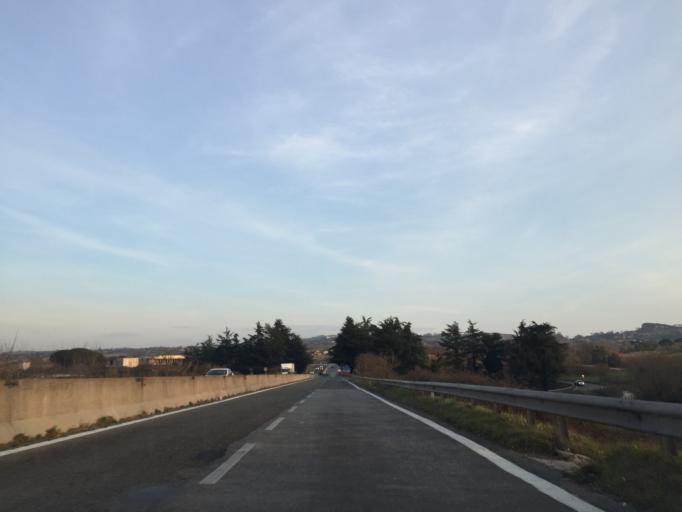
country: IT
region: Latium
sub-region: Citta metropolitana di Roma Capitale
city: Campagnano di Roma
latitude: 42.1562
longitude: 12.3430
